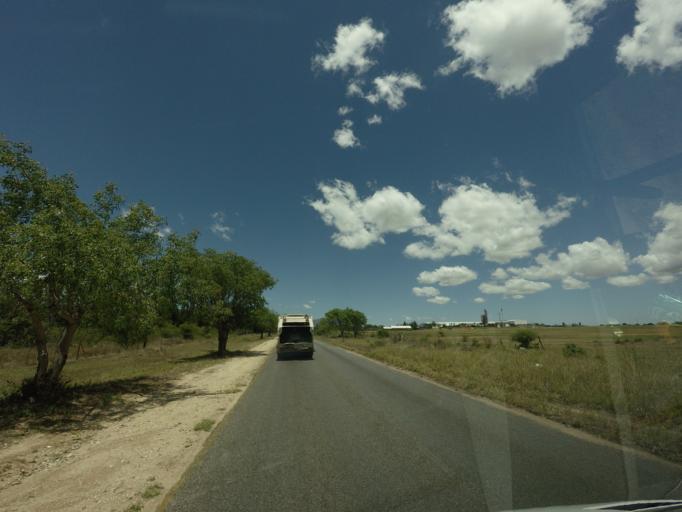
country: ZA
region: Limpopo
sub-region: Mopani District Municipality
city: Hoedspruit
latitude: -24.3835
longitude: 30.8729
